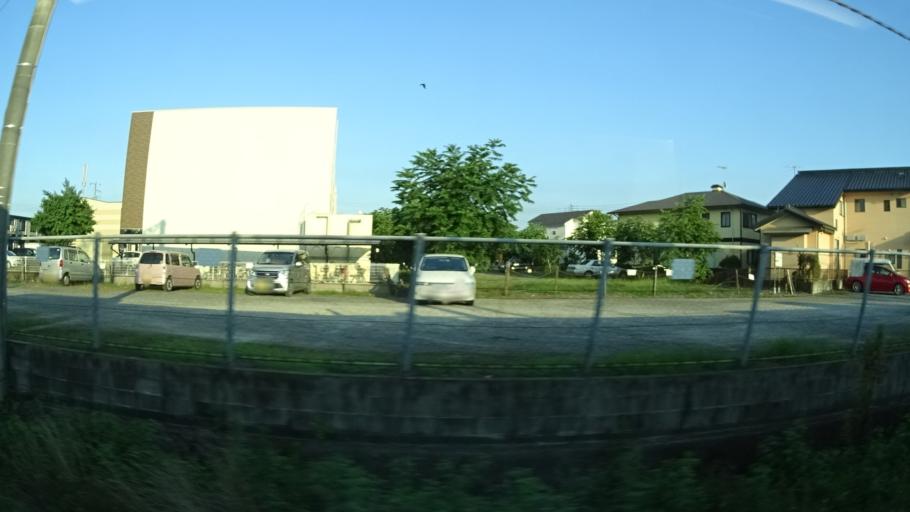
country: JP
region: Ibaraki
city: Ishioka
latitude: 36.1223
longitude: 140.2508
